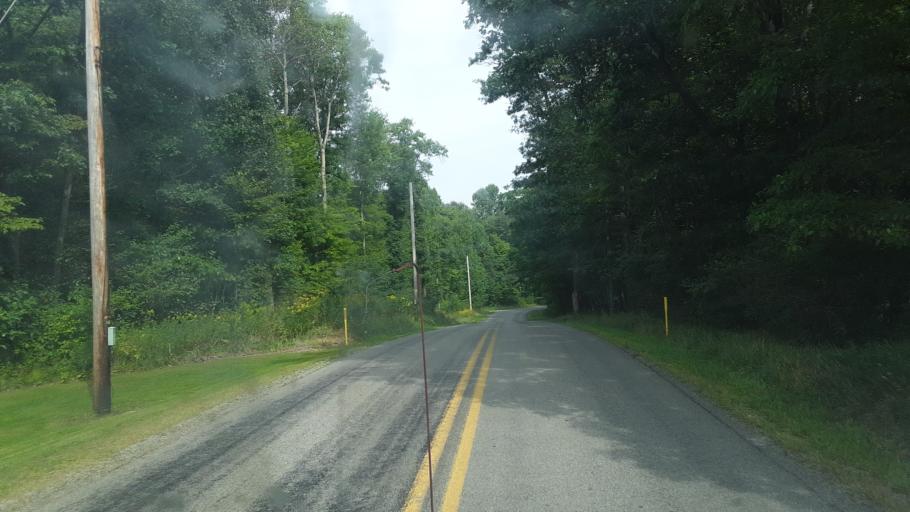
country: US
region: Pennsylvania
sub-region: Jefferson County
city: Punxsutawney
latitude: 40.9498
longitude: -79.0719
